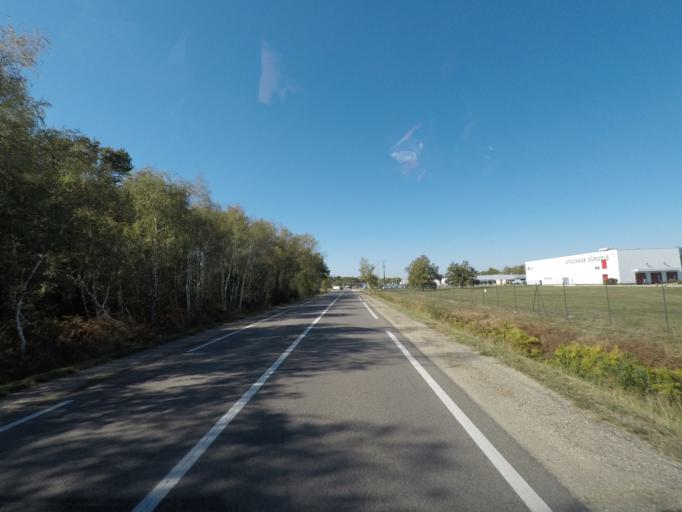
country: FR
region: Rhone-Alpes
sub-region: Departement de l'Ain
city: Attignat
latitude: 46.2596
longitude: 5.1734
